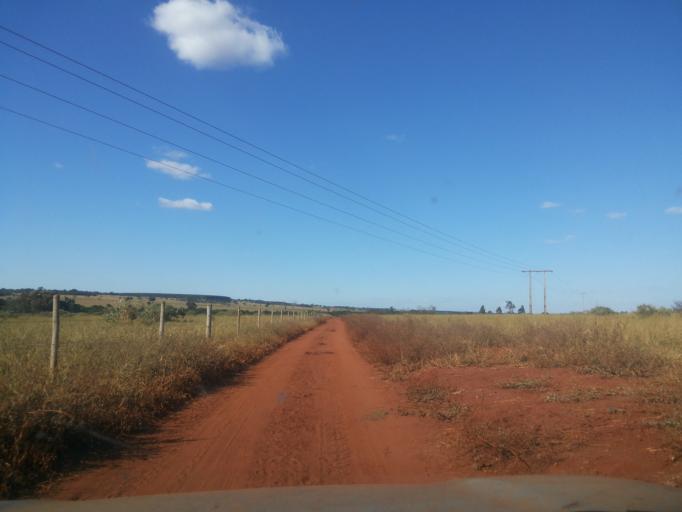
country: BR
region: Minas Gerais
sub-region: Centralina
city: Centralina
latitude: -18.7364
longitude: -49.1774
